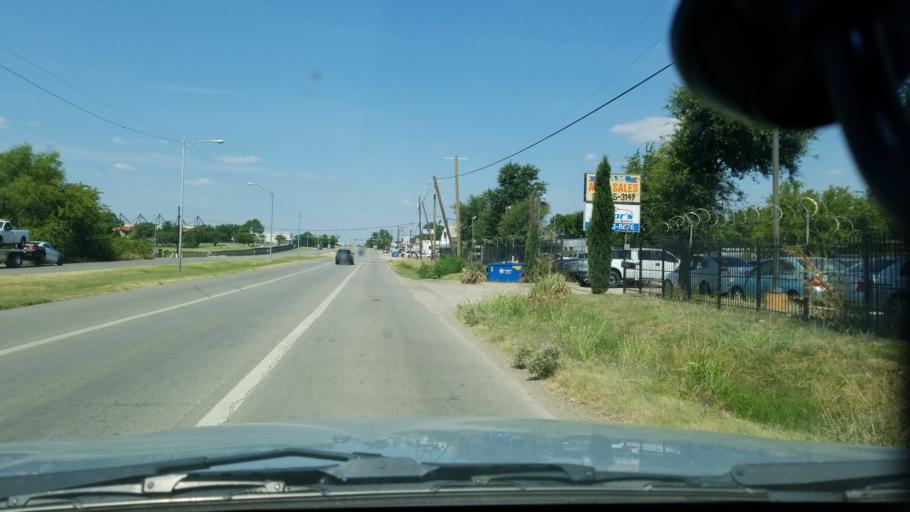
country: US
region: Texas
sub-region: Dallas County
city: Grand Prairie
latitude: 32.7464
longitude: -96.9587
